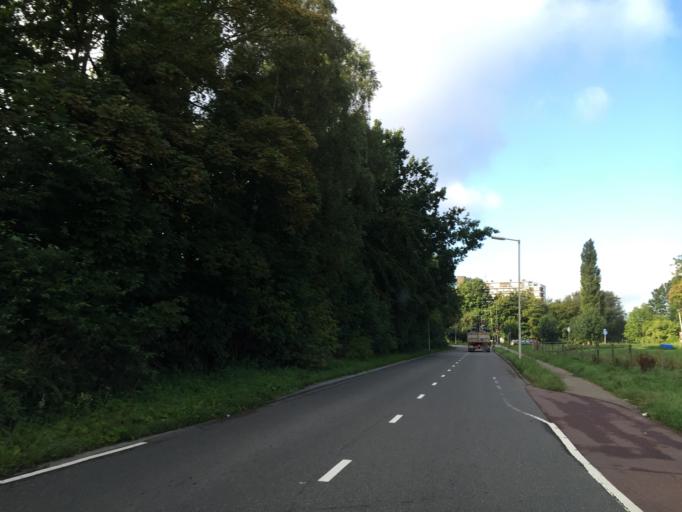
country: NL
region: South Holland
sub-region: Gemeente Schiedam
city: Schiedam
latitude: 51.9462
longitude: 4.4279
